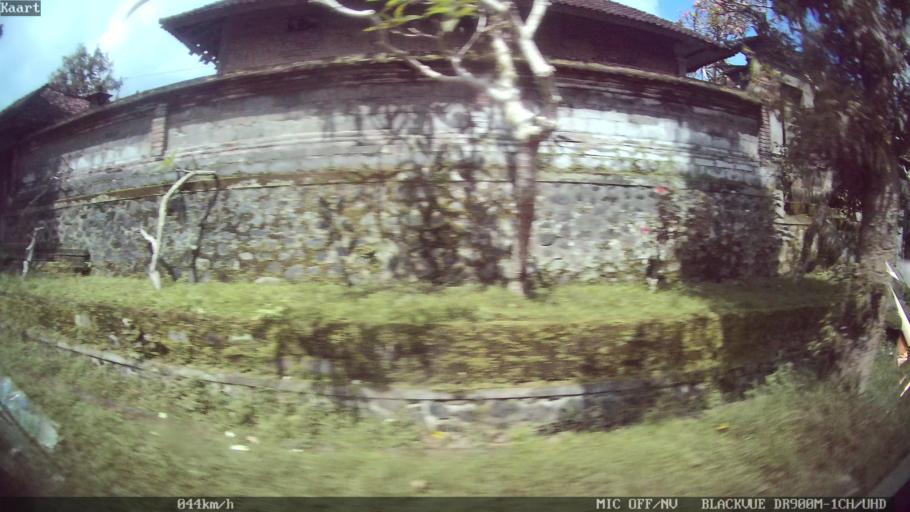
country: ID
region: Bali
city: Banjar Mulung
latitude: -8.4926
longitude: 115.3208
